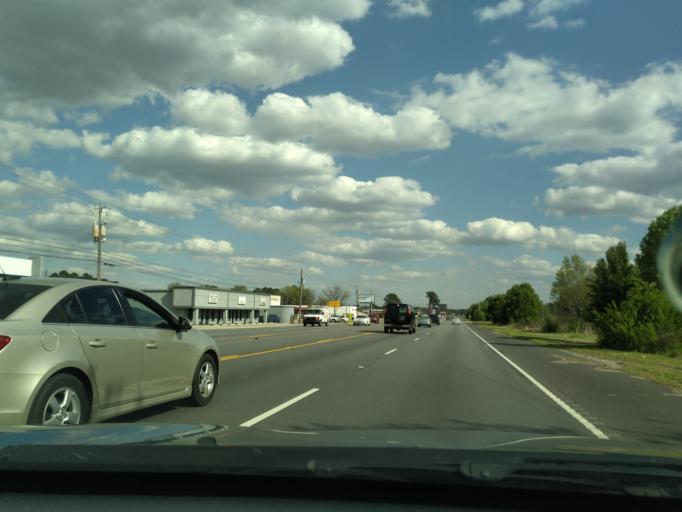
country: US
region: South Carolina
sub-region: Florence County
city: Florence
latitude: 34.2167
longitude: -79.7833
